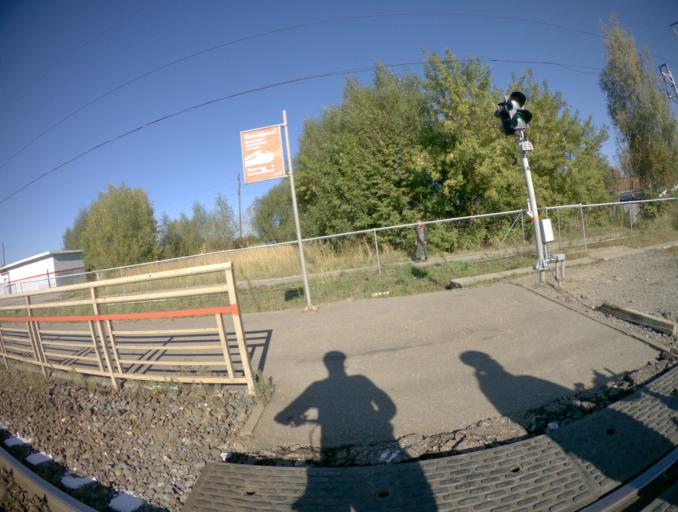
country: RU
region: Vladimir
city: Kameshkovo
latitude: 56.3435
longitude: 40.9912
